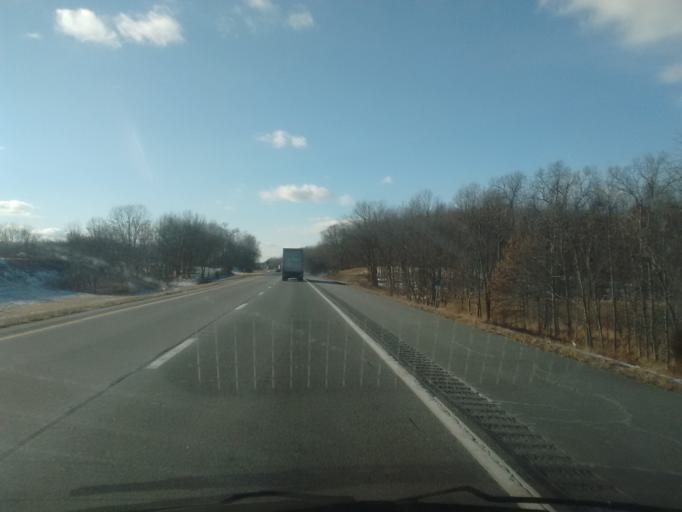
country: US
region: New York
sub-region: Orange County
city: Walden
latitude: 41.5176
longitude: -74.1707
